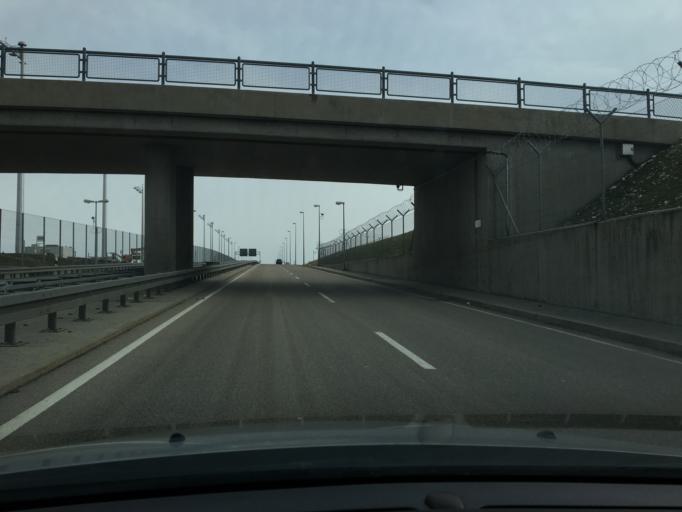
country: DE
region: Bavaria
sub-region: Upper Bavaria
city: Hallbergmoos
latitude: 48.3490
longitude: 11.7971
